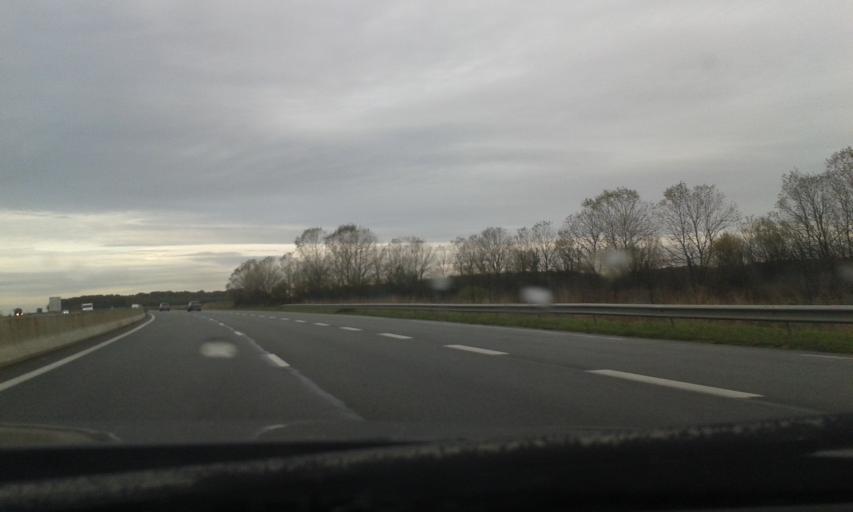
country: FR
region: Centre
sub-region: Departement d'Eure-et-Loir
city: Vernouillet
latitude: 48.6788
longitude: 1.3832
